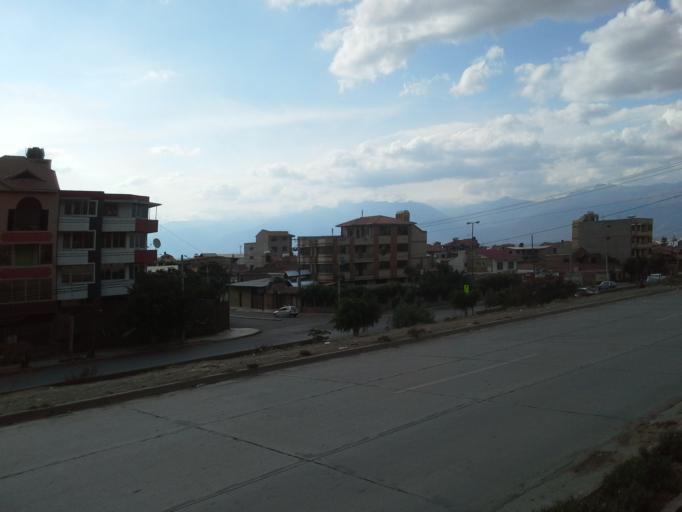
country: BO
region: Cochabamba
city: Cochabamba
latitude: -17.4260
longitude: -66.1538
